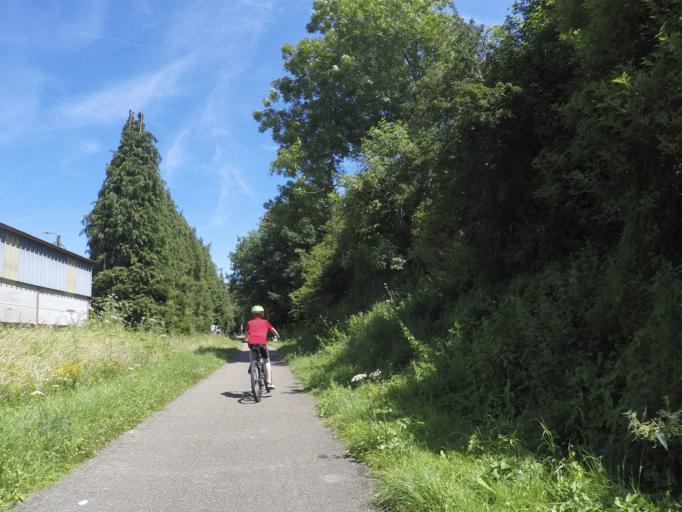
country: BE
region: Wallonia
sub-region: Province de Namur
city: Ciney
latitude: 50.3236
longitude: 5.1228
